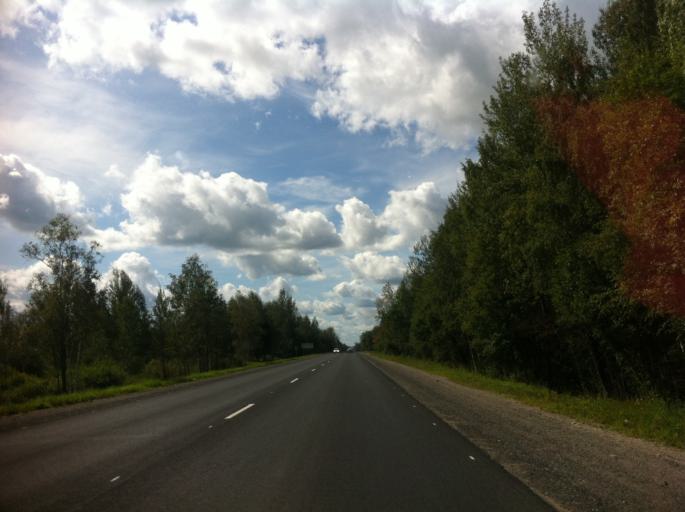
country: RU
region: Pskov
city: Izborsk
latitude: 57.7547
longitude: 28.0661
